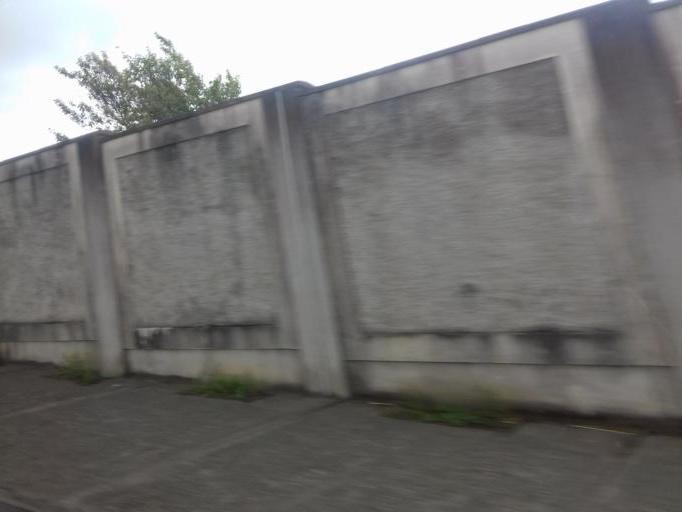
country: IE
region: Leinster
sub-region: Loch Garman
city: Loch Garman
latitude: 52.3409
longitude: -6.4778
